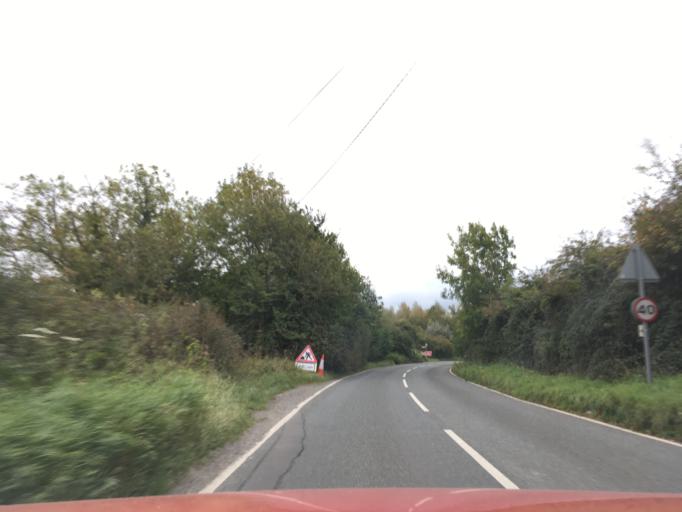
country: GB
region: England
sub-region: Gloucestershire
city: Stonehouse
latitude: 51.7589
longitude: -2.3141
